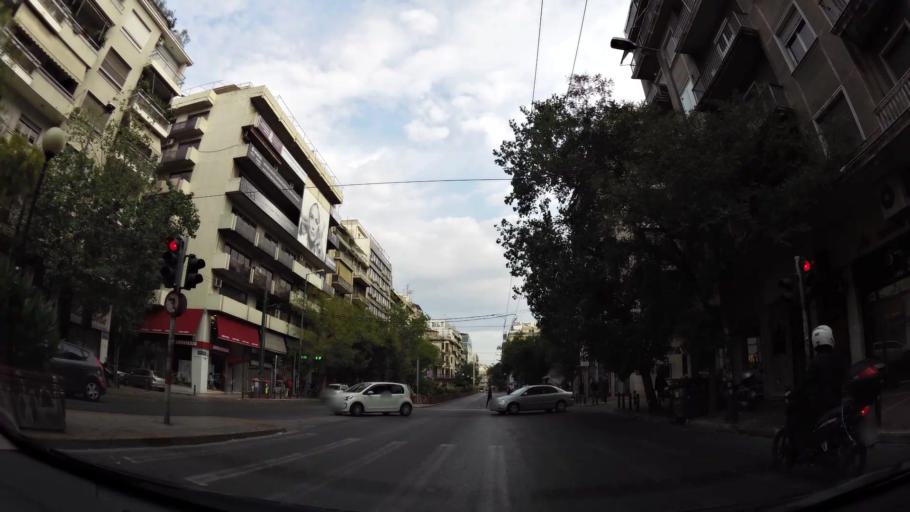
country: GR
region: Attica
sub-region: Nomarchia Athinas
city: Kipseli
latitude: 37.9988
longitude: 23.7331
